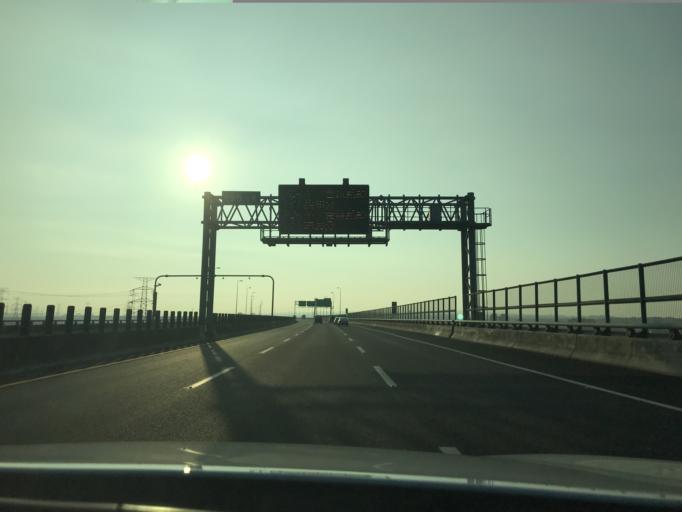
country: TW
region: Taiwan
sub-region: Changhua
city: Chang-hua
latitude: 24.1136
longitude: 120.5426
